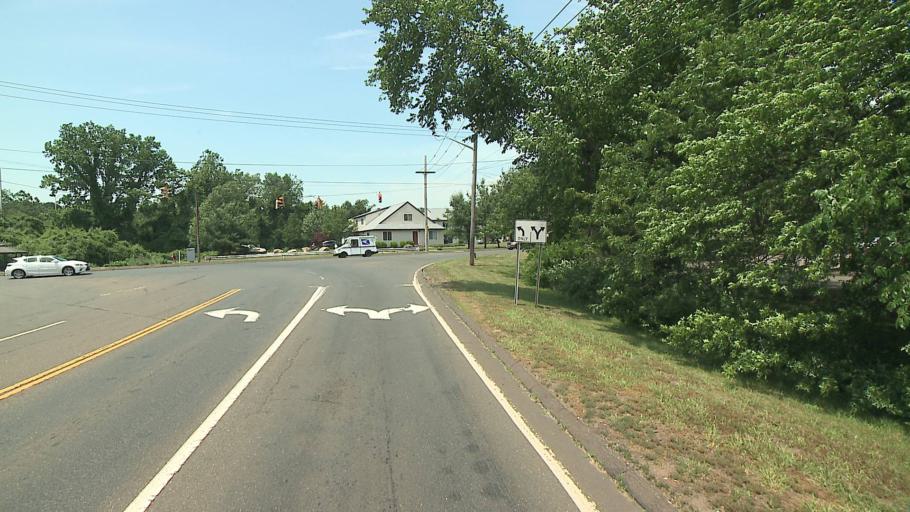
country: US
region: Connecticut
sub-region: New Haven County
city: Hamden
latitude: 41.3816
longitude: -72.8823
